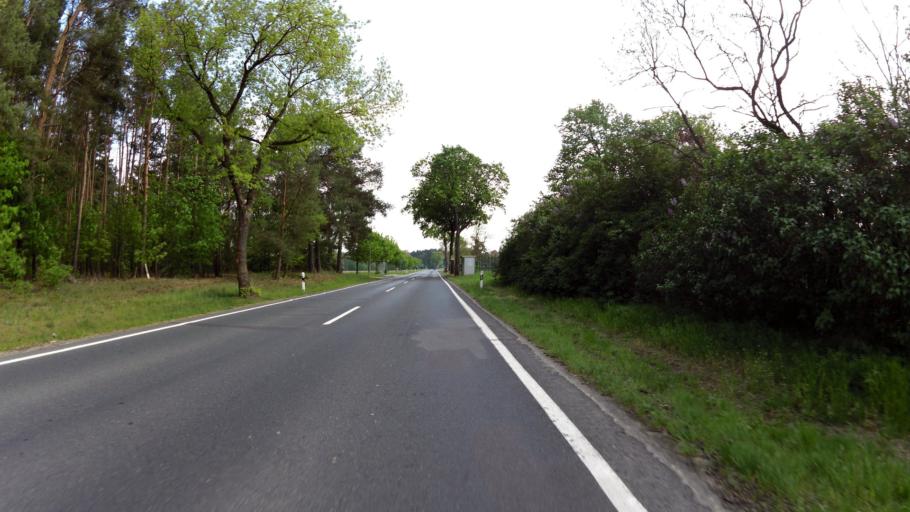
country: DE
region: Brandenburg
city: Spreenhagen
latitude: 52.3285
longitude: 13.8986
